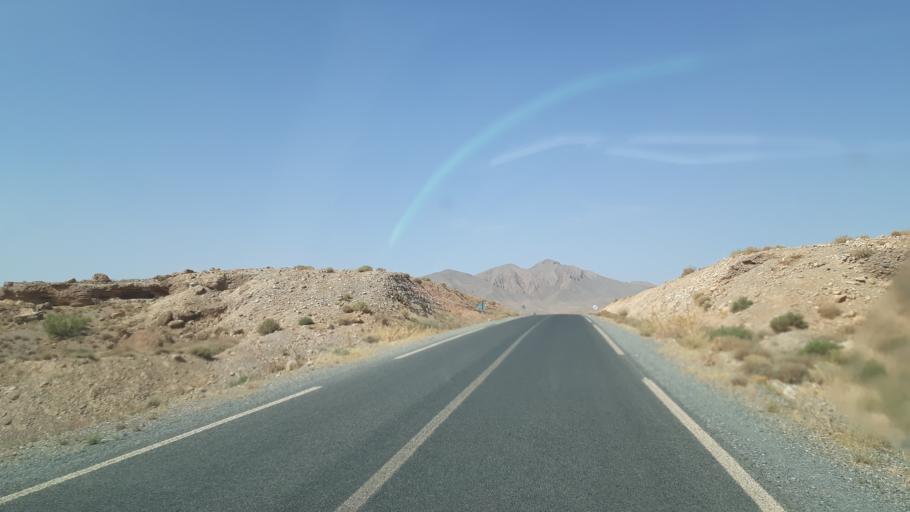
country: MA
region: Meknes-Tafilalet
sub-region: Errachidia
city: Amouguer
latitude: 32.2274
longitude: -4.6675
